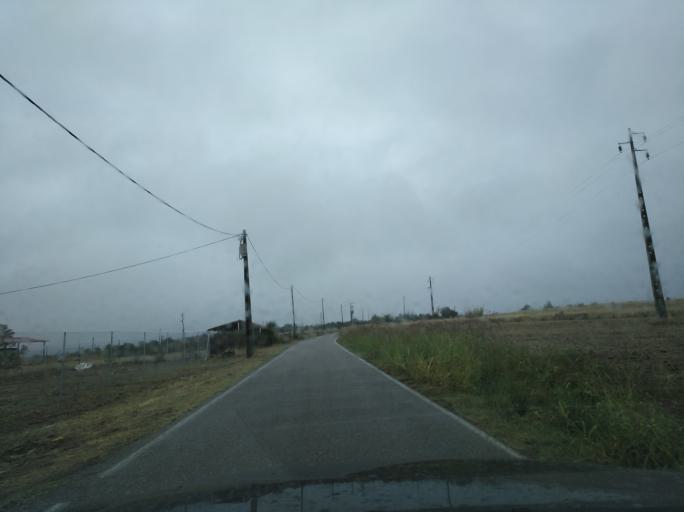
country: PT
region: Portalegre
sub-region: Campo Maior
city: Campo Maior
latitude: 38.9542
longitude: -7.0846
